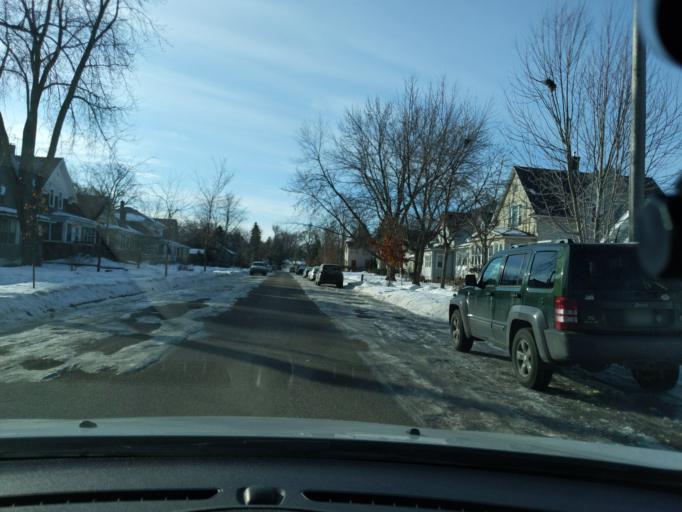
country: US
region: Minnesota
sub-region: Ramsey County
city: Lauderdale
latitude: 44.9893
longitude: -93.2177
